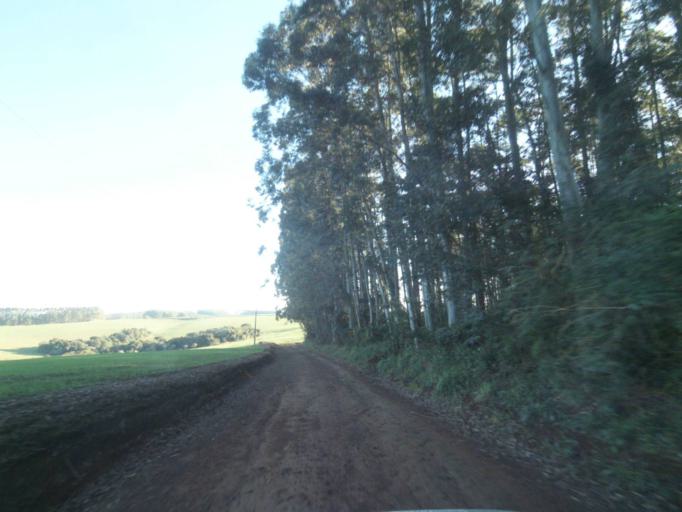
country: BR
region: Parana
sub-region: Telemaco Borba
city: Telemaco Borba
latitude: -24.4788
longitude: -50.5891
